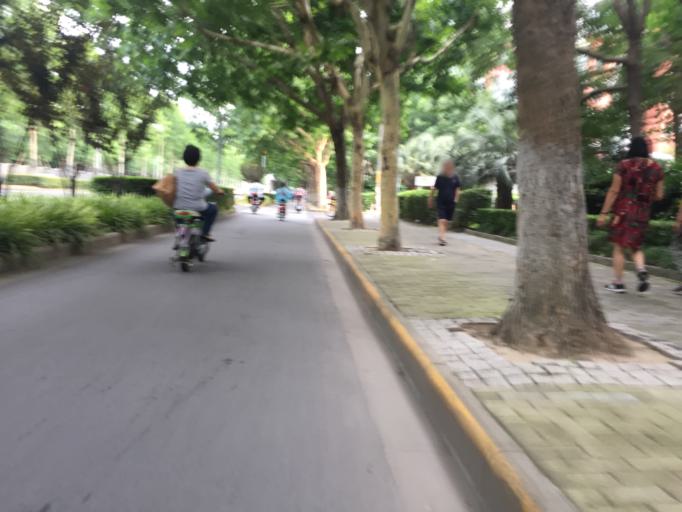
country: CN
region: Shanghai Shi
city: Huamu
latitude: 31.1849
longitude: 121.5368
